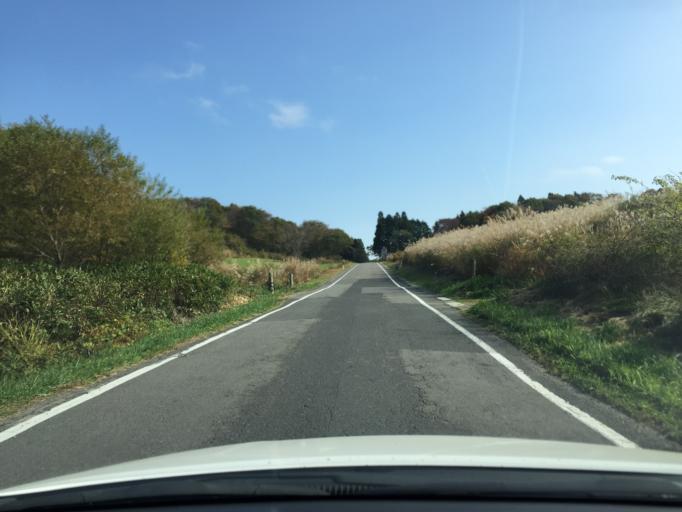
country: JP
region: Fukushima
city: Ishikawa
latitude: 36.9547
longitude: 140.5724
